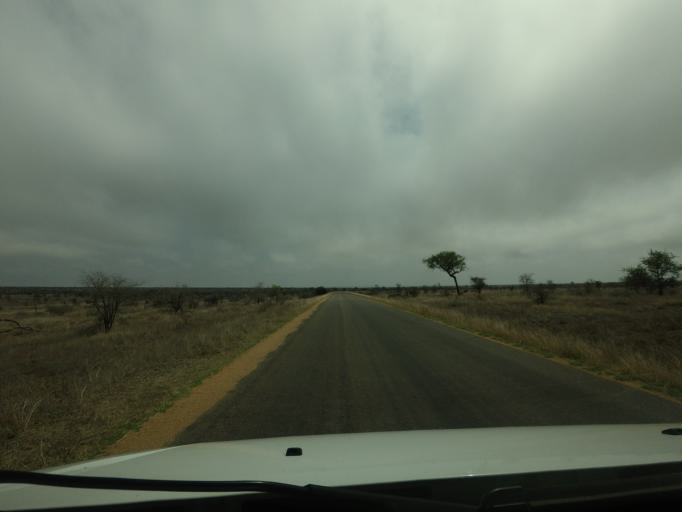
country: ZA
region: Limpopo
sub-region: Mopani District Municipality
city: Phalaborwa
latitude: -24.2022
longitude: 31.7191
